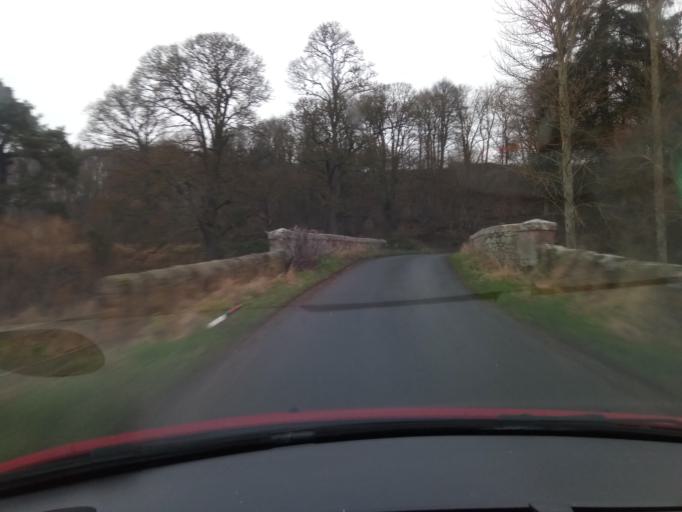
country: GB
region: Scotland
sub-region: The Scottish Borders
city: Kelso
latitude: 55.5368
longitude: -2.4505
